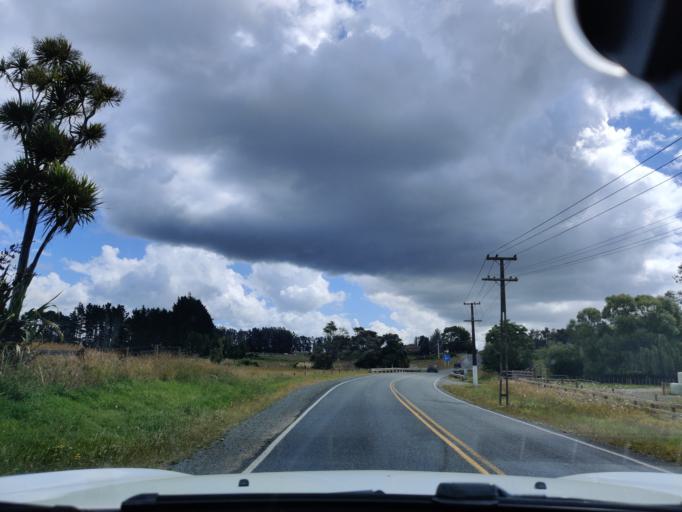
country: NZ
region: Auckland
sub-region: Auckland
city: Red Hill
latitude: -37.0391
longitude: 174.9920
